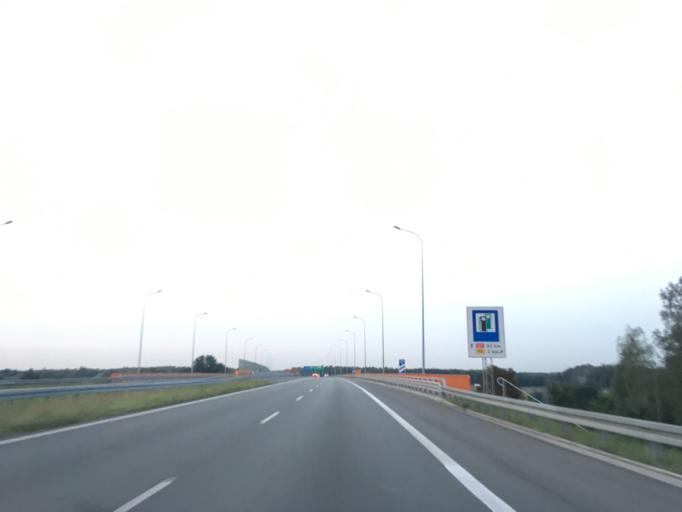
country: PL
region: Lodz Voivodeship
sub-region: Powiat lodzki wschodni
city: Andrespol
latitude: 51.7528
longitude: 19.5954
